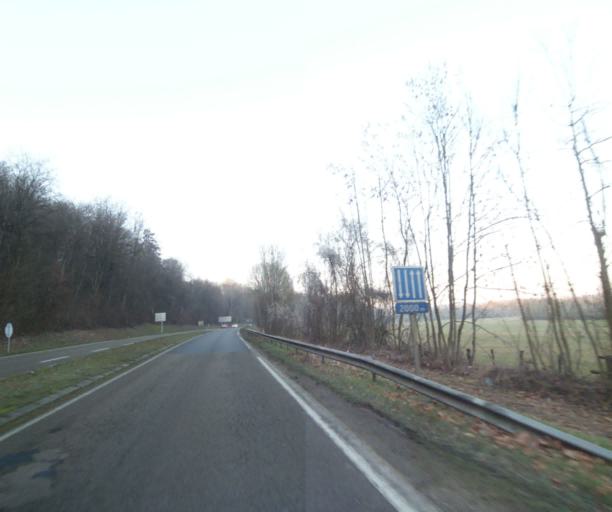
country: FR
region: Champagne-Ardenne
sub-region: Departement de la Haute-Marne
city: Bienville
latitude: 48.5932
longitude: 5.0311
